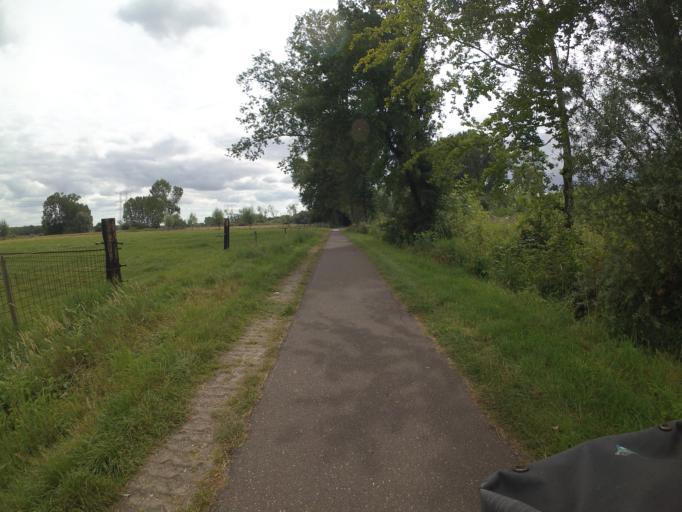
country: NL
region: North Brabant
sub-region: Gemeente Son en Breugel
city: Son
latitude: 51.4890
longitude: 5.5052
